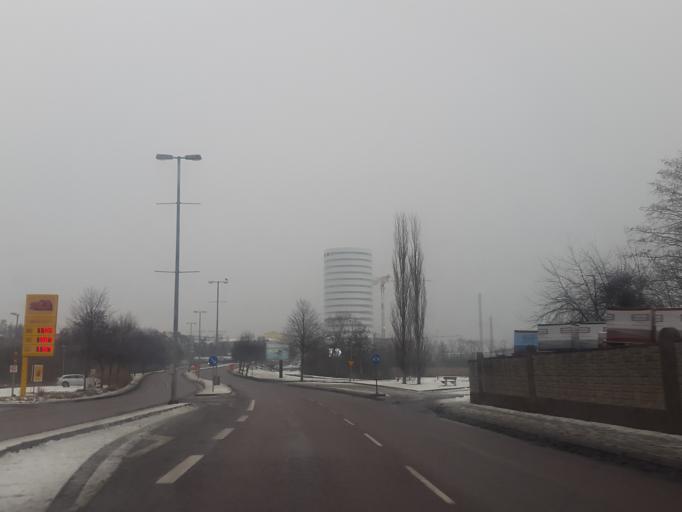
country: SE
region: Joenkoeping
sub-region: Jonkopings Kommun
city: Jonkoping
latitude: 57.7651
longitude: 14.1535
